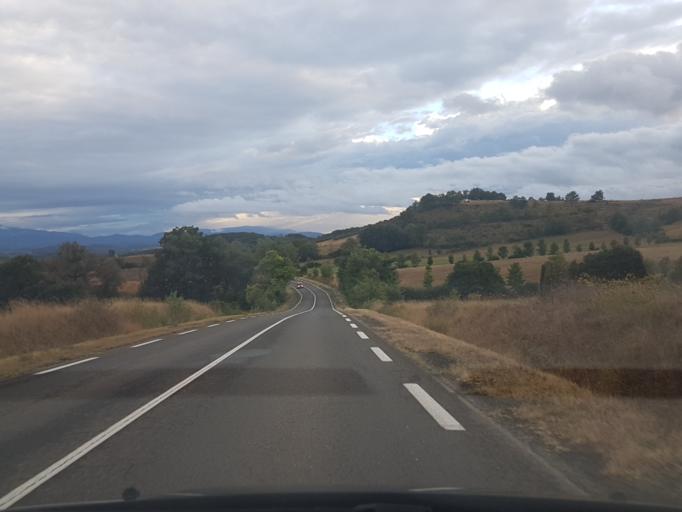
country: FR
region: Midi-Pyrenees
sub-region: Departement de l'Ariege
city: Mirepoix
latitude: 43.1283
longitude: 1.9434
